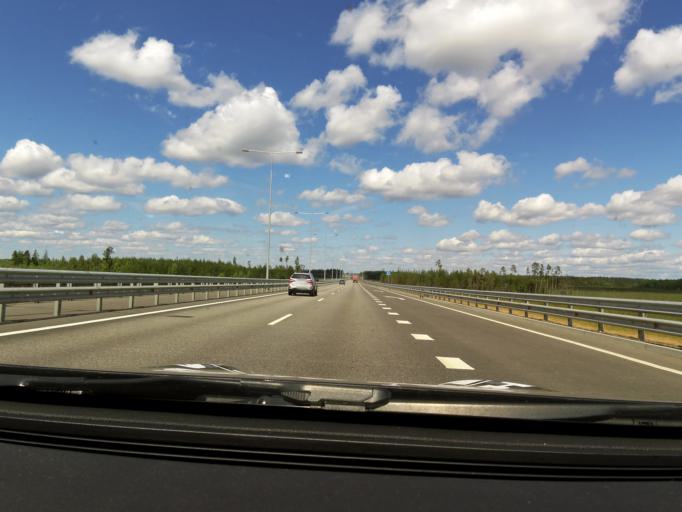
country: RU
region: Tverskaya
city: Krasnomayskiy
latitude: 57.6837
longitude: 34.2201
